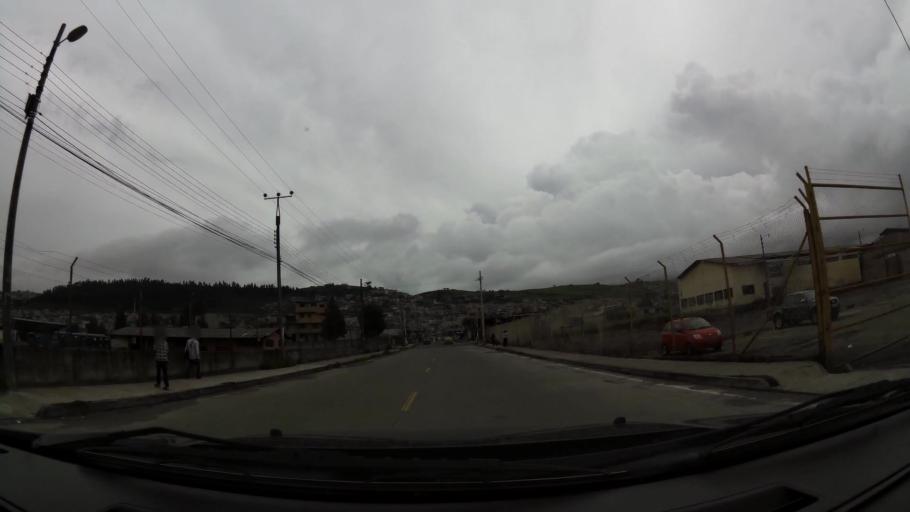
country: EC
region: Pichincha
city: Sangolqui
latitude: -0.3186
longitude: -78.5391
